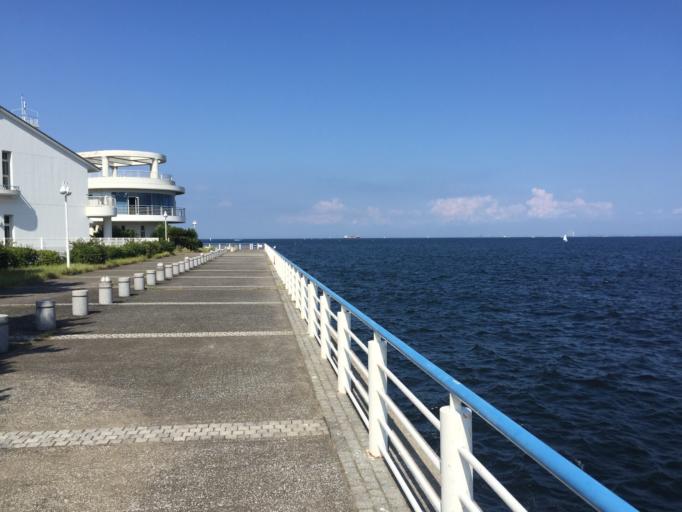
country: JP
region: Kanagawa
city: Yokosuka
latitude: 35.3343
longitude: 139.6480
